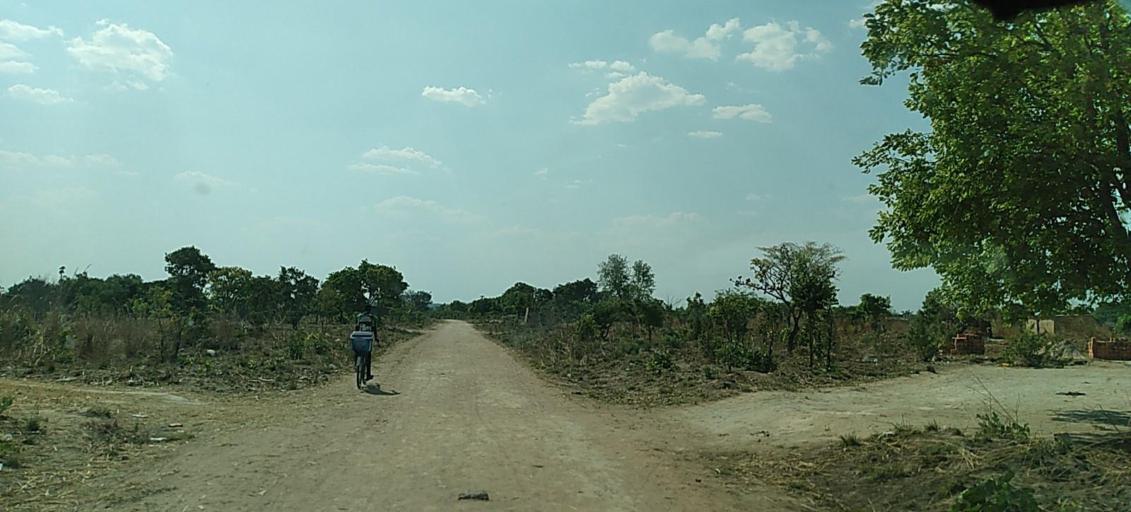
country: ZM
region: North-Western
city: Kalengwa
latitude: -13.1219
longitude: 25.0038
